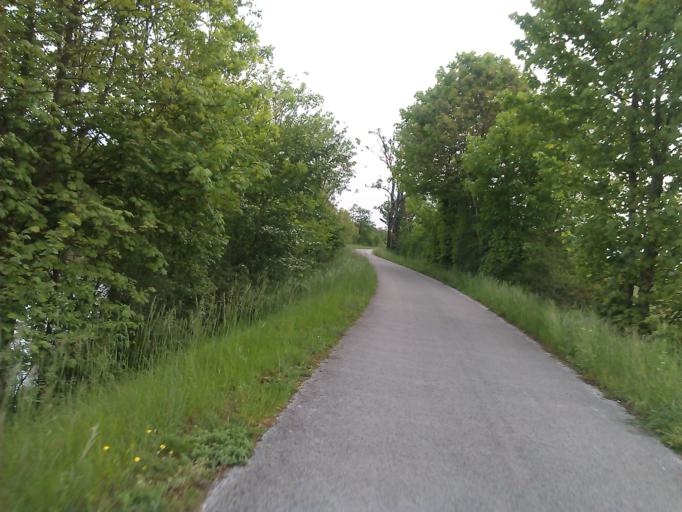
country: FR
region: Franche-Comte
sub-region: Departement du Jura
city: Fraisans
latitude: 47.1648
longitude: 5.7796
